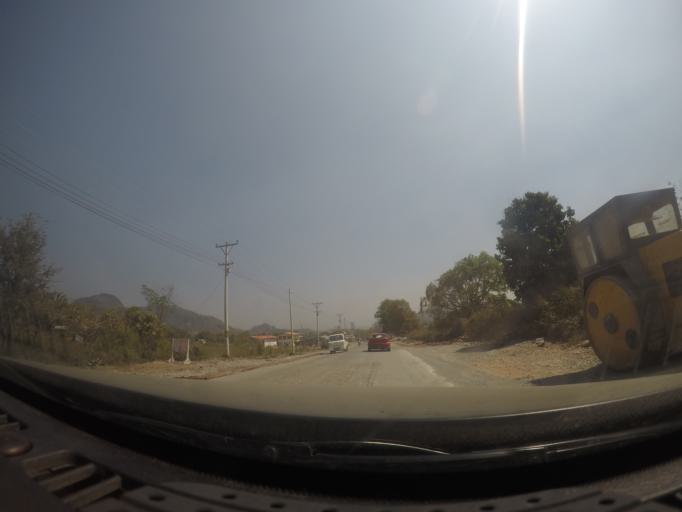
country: MM
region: Shan
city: Taunggyi
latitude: 20.7738
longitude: 97.1252
